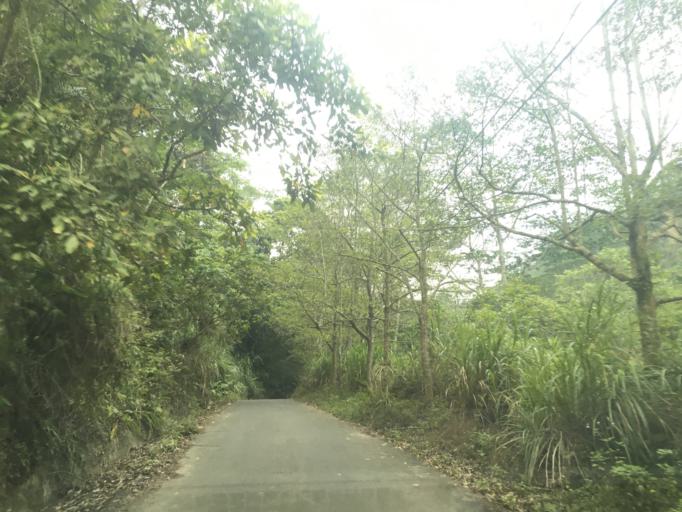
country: TW
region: Taiwan
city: Zhongxing New Village
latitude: 24.0476
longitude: 120.7861
